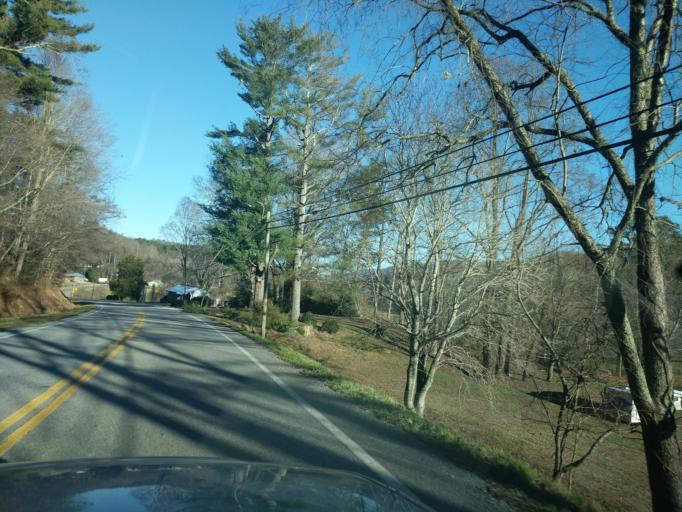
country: US
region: Georgia
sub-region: Rabun County
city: Clayton
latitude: 34.8782
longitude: -83.4348
